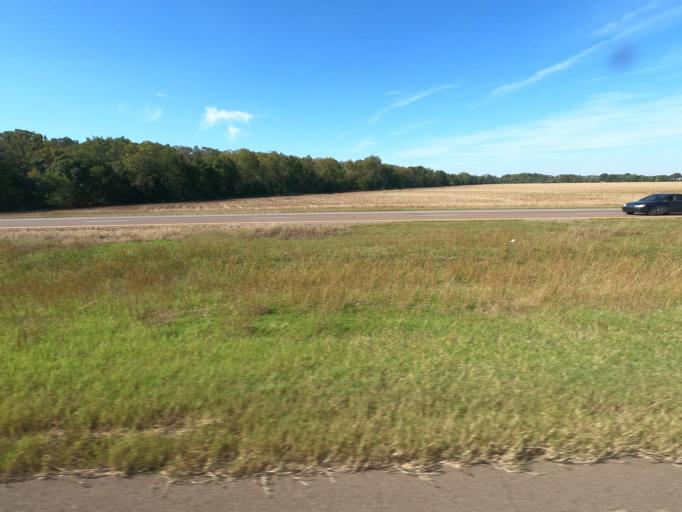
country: US
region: Tennessee
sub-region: Dyer County
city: Dyersburg
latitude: 36.0370
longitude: -89.3386
